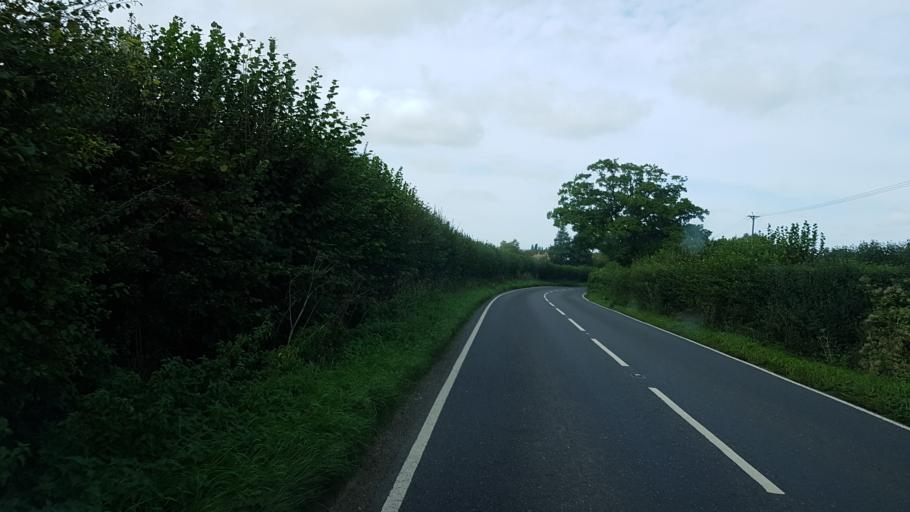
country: GB
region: England
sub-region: Kent
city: Maidstone
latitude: 51.2271
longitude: 0.5569
